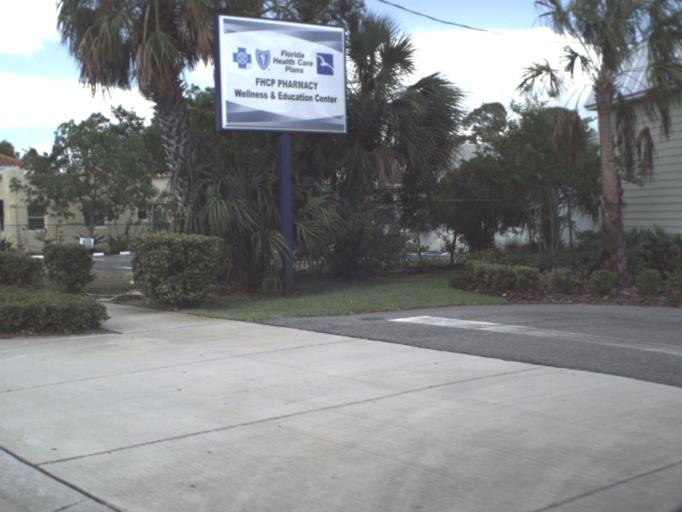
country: US
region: Florida
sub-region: Brevard County
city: Titusville
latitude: 28.6046
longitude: -80.8076
